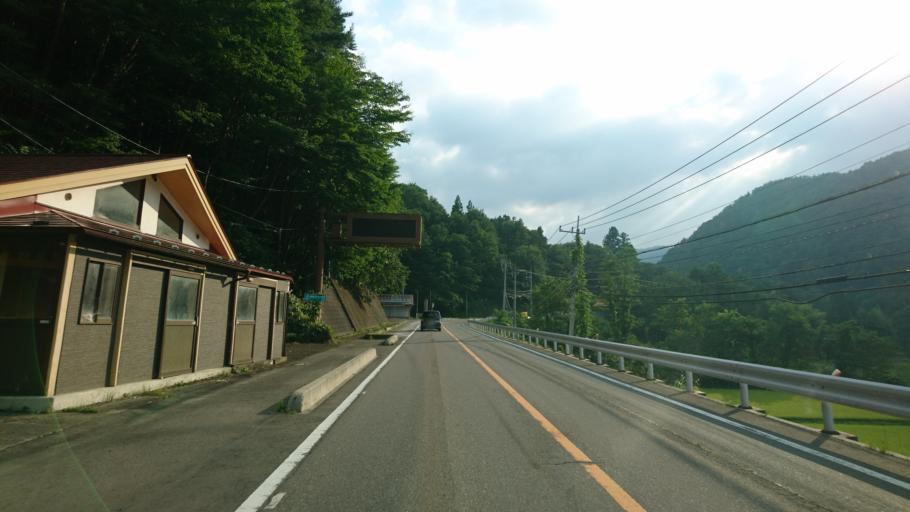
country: JP
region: Gunma
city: Numata
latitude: 36.7364
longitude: 139.2294
